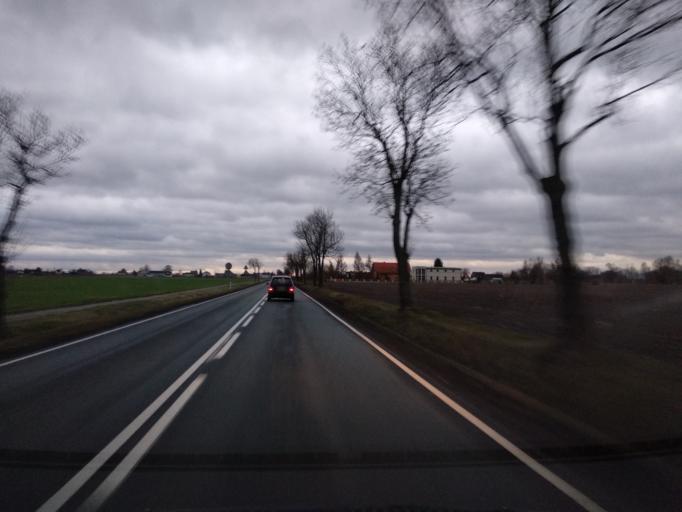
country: PL
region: Greater Poland Voivodeship
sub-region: Powiat koninski
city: Rychwal
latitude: 52.0640
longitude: 18.1638
